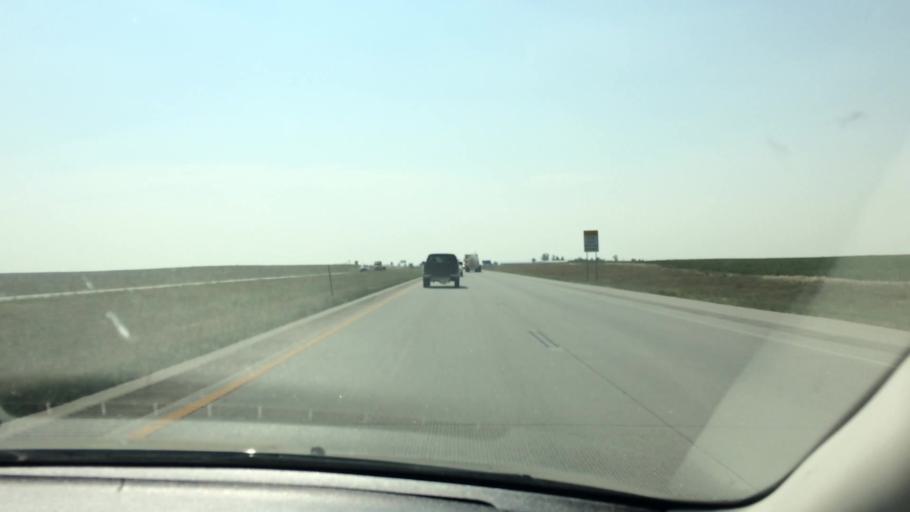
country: US
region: Colorado
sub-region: Adams County
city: Bennett
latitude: 39.7386
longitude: -104.5093
